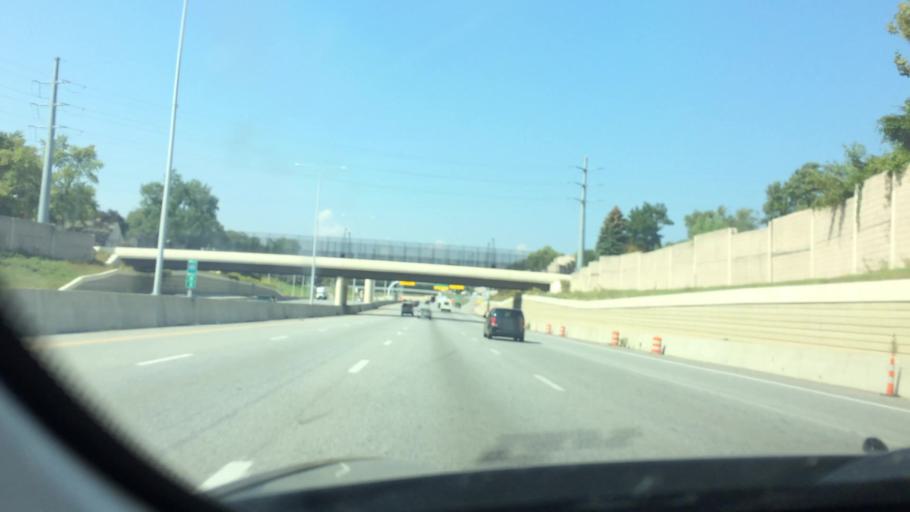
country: US
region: Ohio
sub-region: Lucas County
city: Toledo
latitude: 41.6829
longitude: -83.5980
